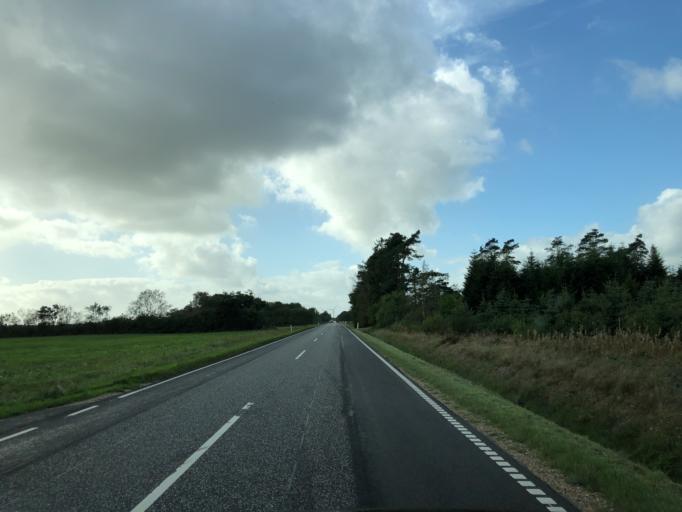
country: DK
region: Central Jutland
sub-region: Holstebro Kommune
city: Holstebro
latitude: 56.3712
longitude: 8.5385
